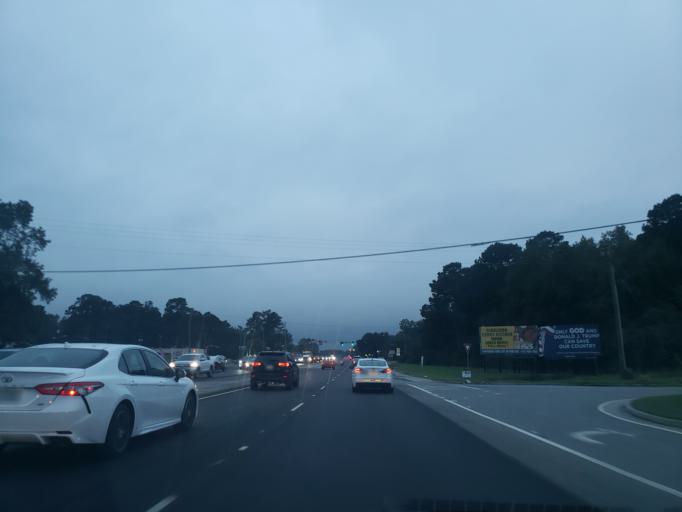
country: US
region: Georgia
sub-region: Chatham County
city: Georgetown
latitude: 31.9977
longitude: -81.2576
